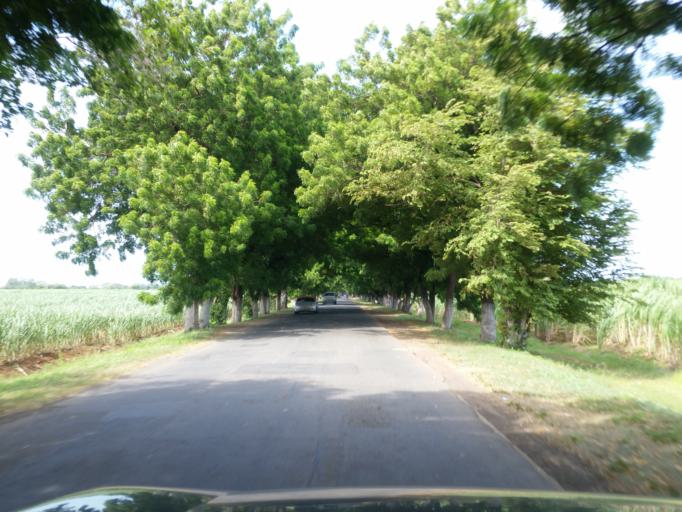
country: NI
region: Managua
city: Masachapa
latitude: 11.7995
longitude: -86.4999
